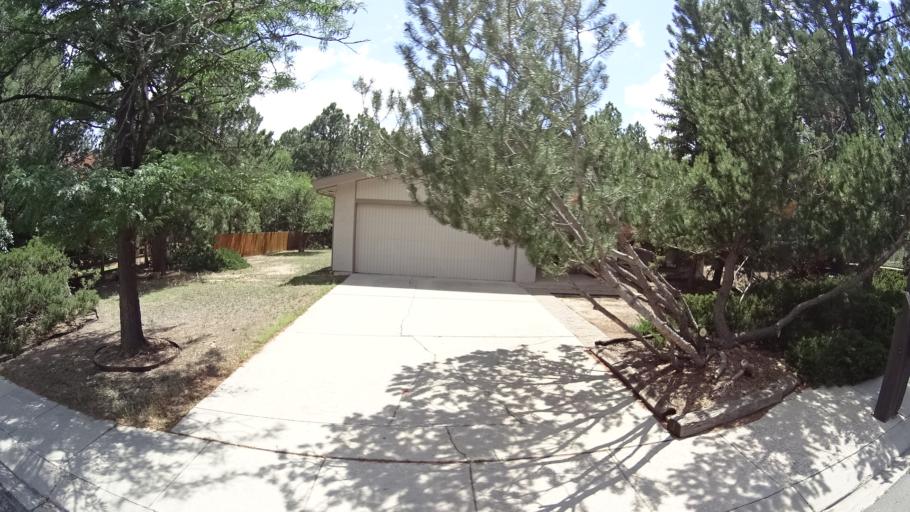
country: US
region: Colorado
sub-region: El Paso County
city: Air Force Academy
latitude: 38.9365
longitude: -104.8394
